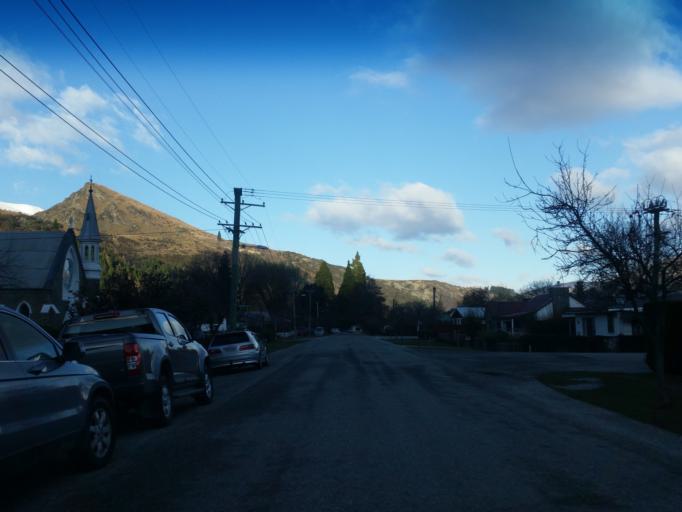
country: NZ
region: Otago
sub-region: Queenstown-Lakes District
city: Arrowtown
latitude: -44.9399
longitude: 168.8332
